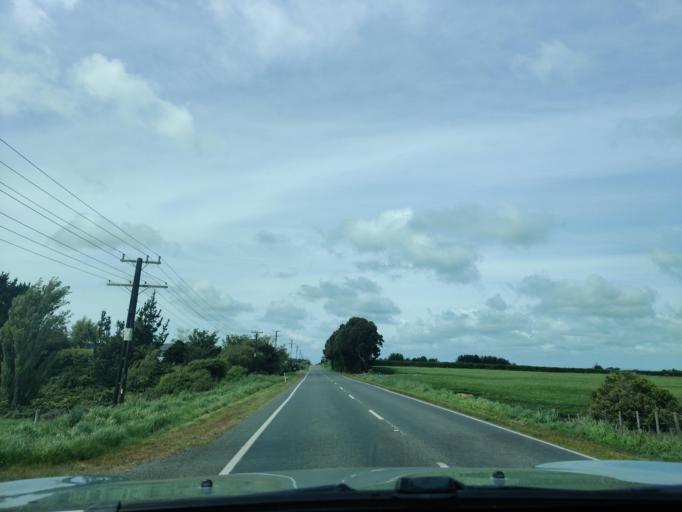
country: NZ
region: Taranaki
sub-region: South Taranaki District
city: Eltham
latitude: -39.4284
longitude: 174.1595
